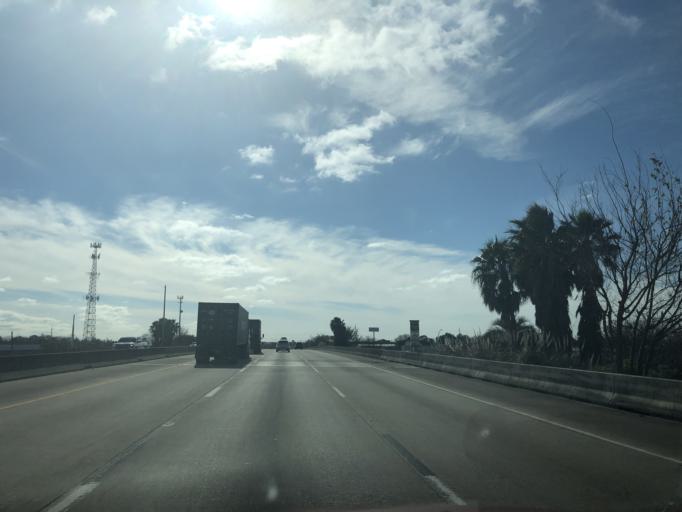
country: US
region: Texas
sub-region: Harris County
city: La Porte
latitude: 29.6662
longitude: -95.0294
